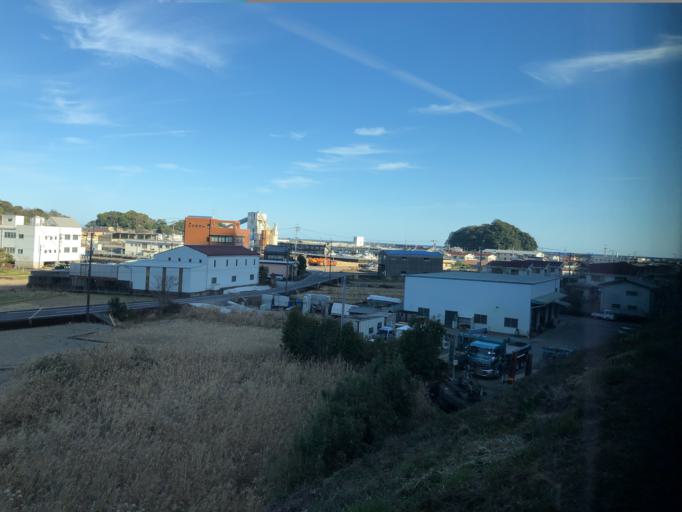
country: JP
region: Kochi
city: Nakamura
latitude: 33.0778
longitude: 133.1029
